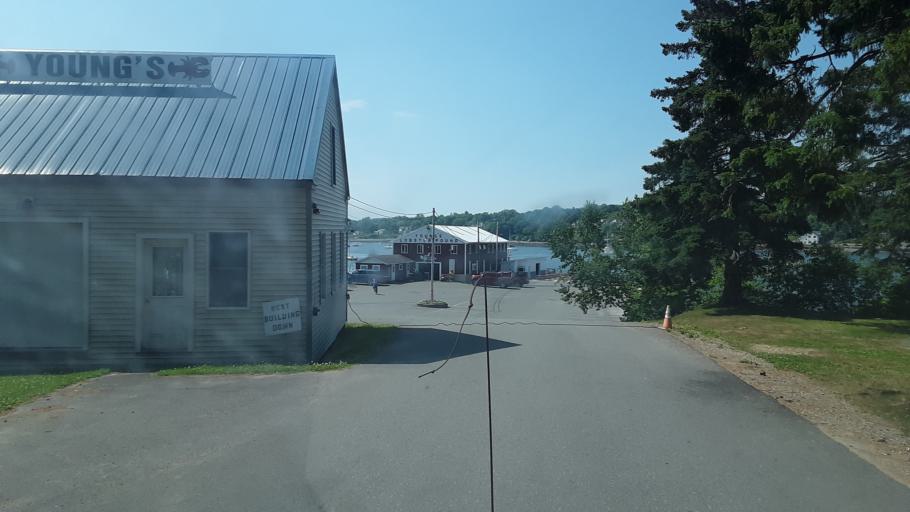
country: US
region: Maine
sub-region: Waldo County
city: Belfast
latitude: 44.4312
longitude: -68.9965
